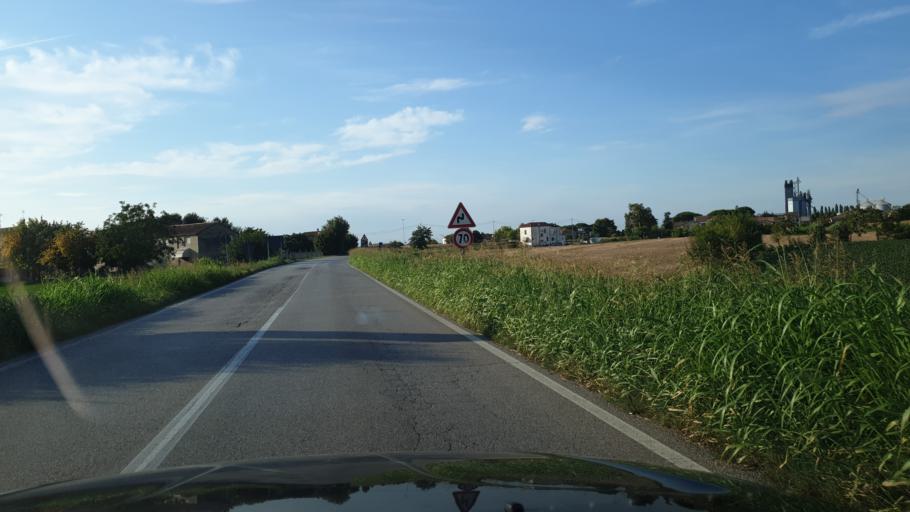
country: IT
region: Veneto
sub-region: Provincia di Rovigo
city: Fiesso Umbertiano
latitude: 44.9668
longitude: 11.6115
